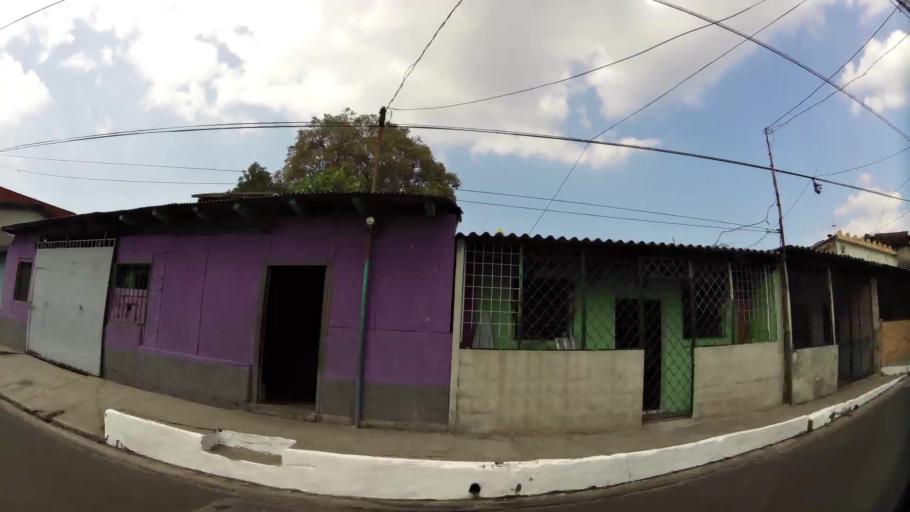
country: SV
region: San Salvador
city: Delgado
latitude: 13.7179
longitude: -89.1654
